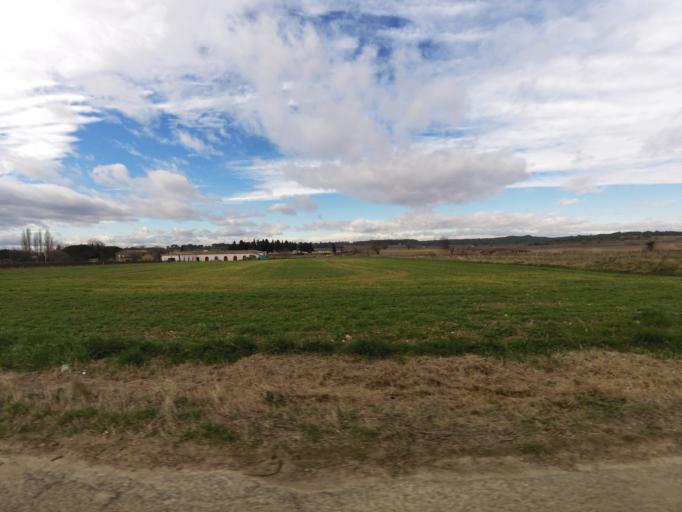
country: FR
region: Languedoc-Roussillon
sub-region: Departement du Gard
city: Aigues-Vives
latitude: 43.7442
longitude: 4.1894
